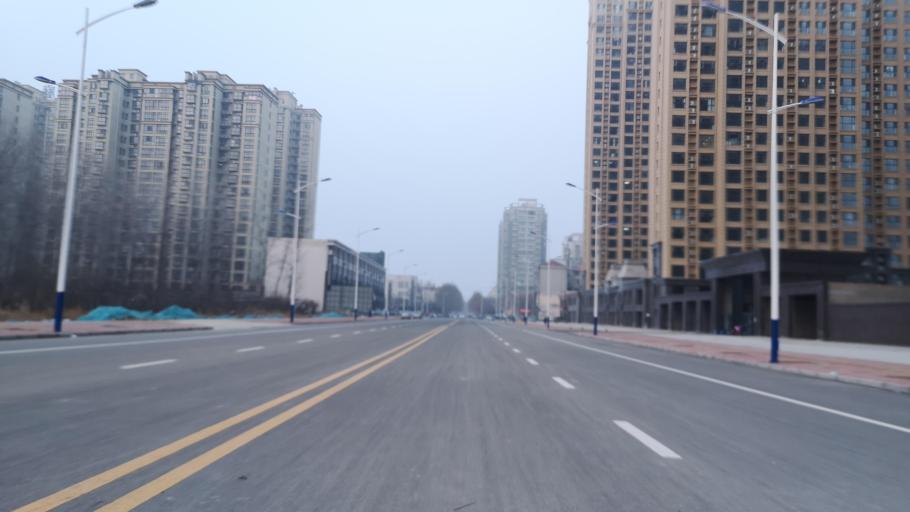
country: CN
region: Henan Sheng
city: Zhongyuanlu
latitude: 35.7507
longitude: 115.0601
